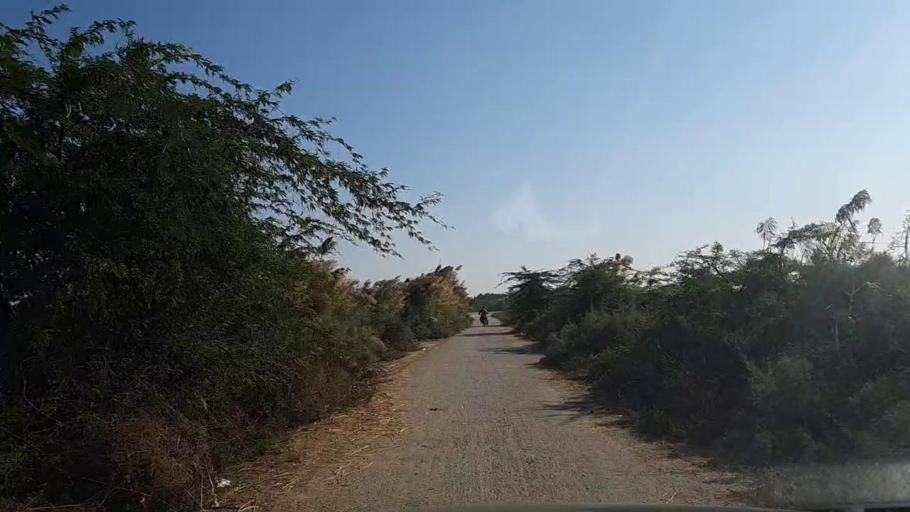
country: PK
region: Sindh
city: Mirpur Batoro
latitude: 24.7278
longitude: 68.2691
